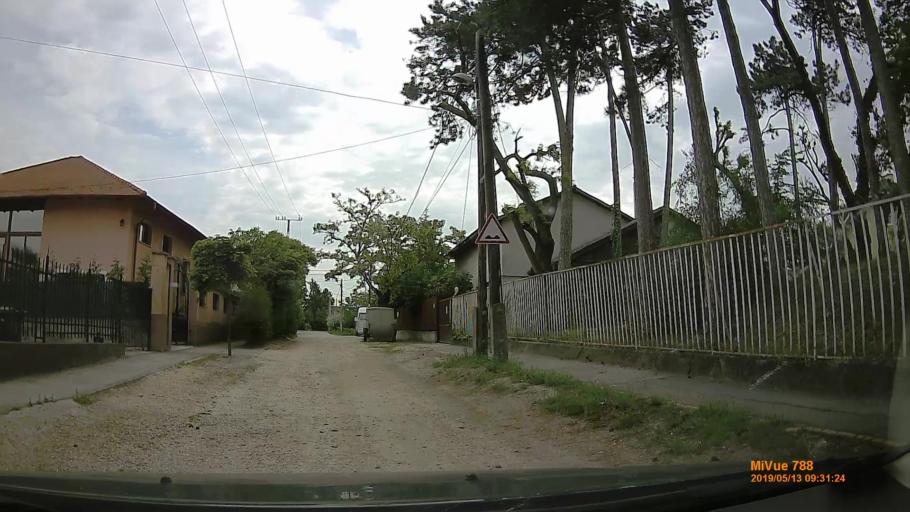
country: HU
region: Budapest
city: Budapest XXIII. keruelet
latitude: 47.4029
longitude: 19.0980
